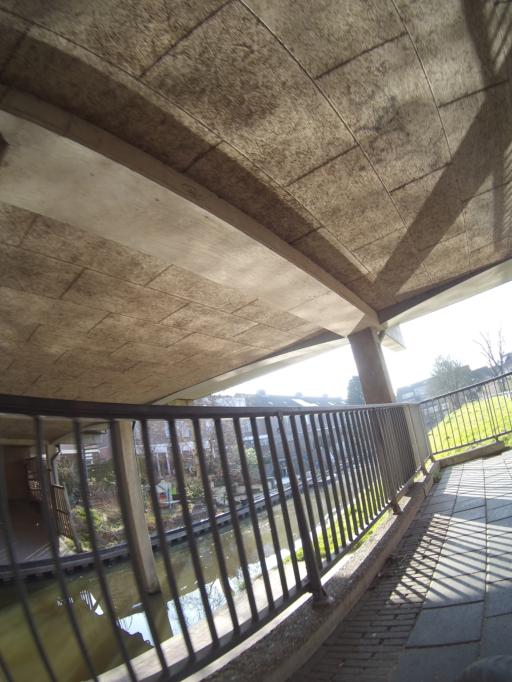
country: NL
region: Utrecht
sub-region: Gemeente Amersfoort
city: Randenbroek
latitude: 52.1559
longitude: 5.3983
